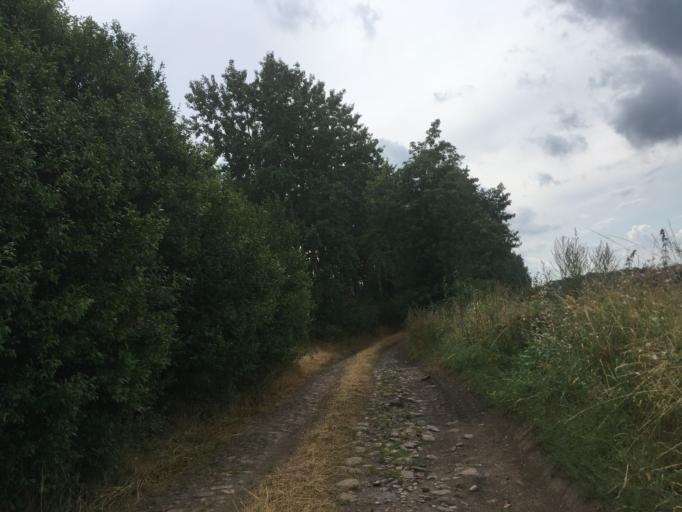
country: DE
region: Brandenburg
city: Chorin
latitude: 52.9464
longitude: 13.8843
